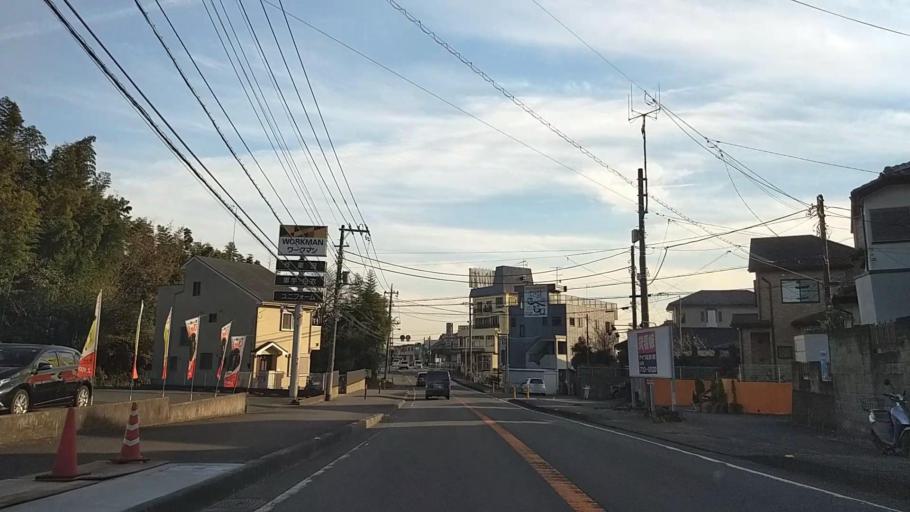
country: JP
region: Kanagawa
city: Atsugi
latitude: 35.4959
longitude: 139.3160
